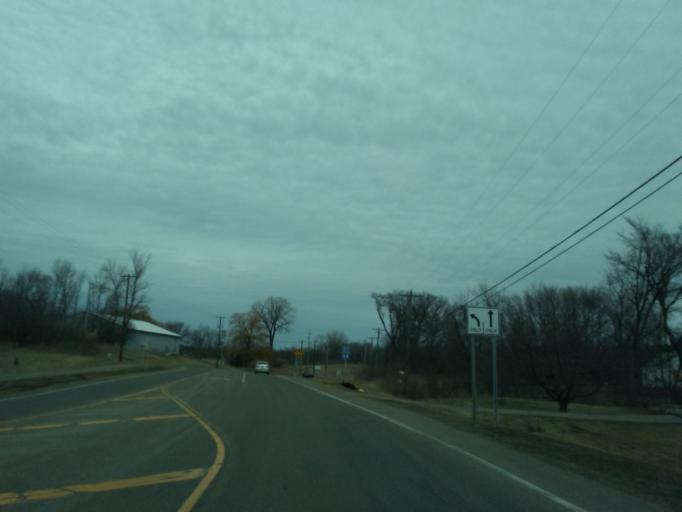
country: US
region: Minnesota
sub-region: Dakota County
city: Inver Grove Heights
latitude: 44.8374
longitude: -93.1009
